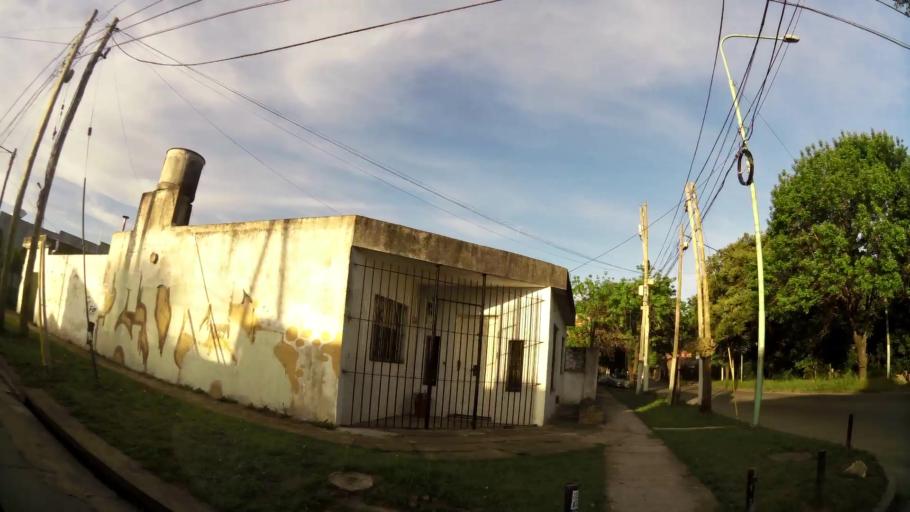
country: AR
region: Buenos Aires
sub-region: Partido de Quilmes
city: Quilmes
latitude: -34.7805
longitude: -58.2003
